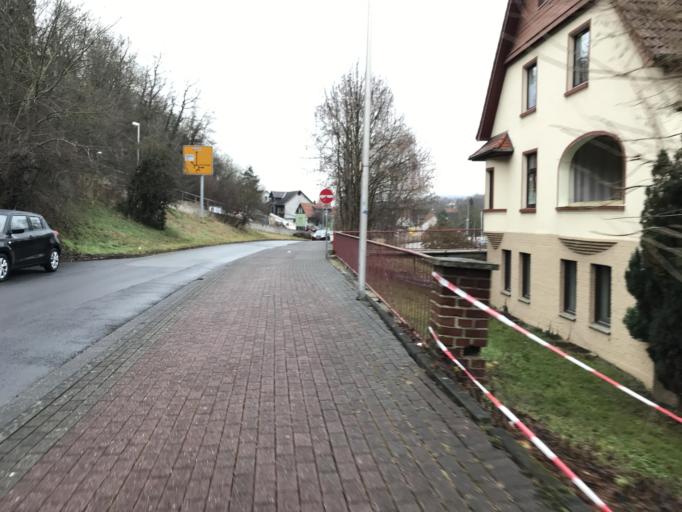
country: DE
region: Hesse
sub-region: Regierungsbezirk Kassel
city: Bad Wildungen
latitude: 51.1176
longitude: 9.1225
